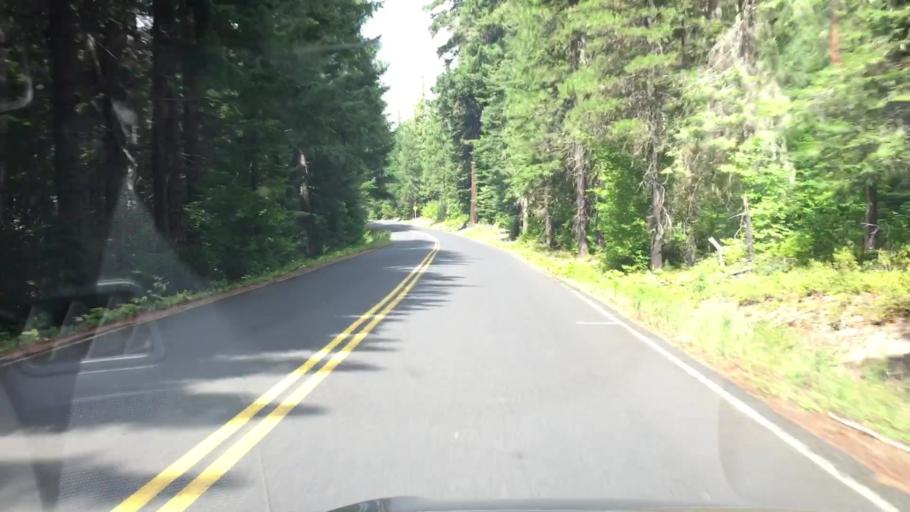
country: US
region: Washington
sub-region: Klickitat County
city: White Salmon
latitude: 46.0688
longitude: -121.5753
